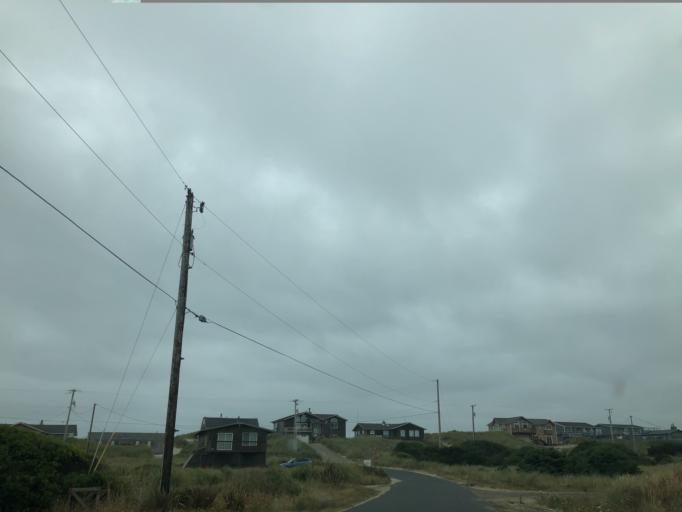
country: US
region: Oregon
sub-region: Lincoln County
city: Waldport
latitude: 44.4305
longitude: -124.0813
